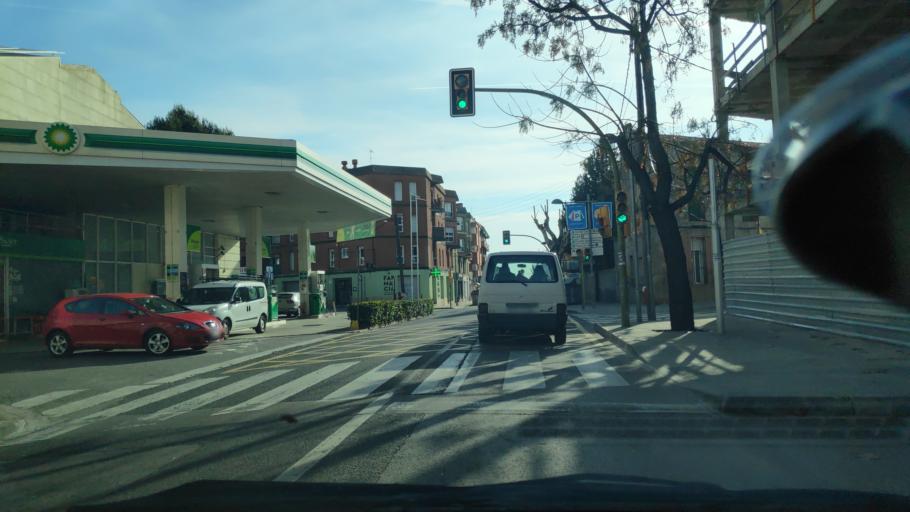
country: ES
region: Catalonia
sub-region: Provincia de Barcelona
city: Castellar del Valles
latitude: 41.6142
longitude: 2.0828
